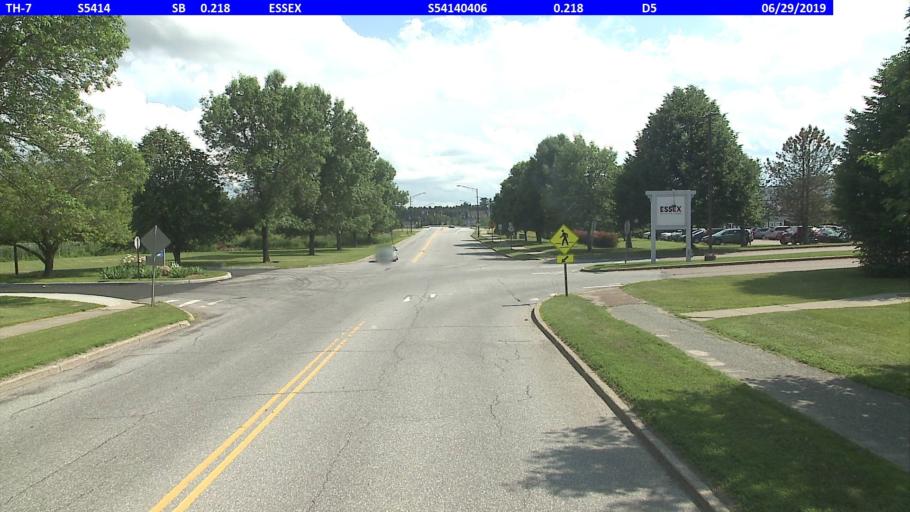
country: US
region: Vermont
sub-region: Chittenden County
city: Essex Junction
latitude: 44.5076
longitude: -73.0790
